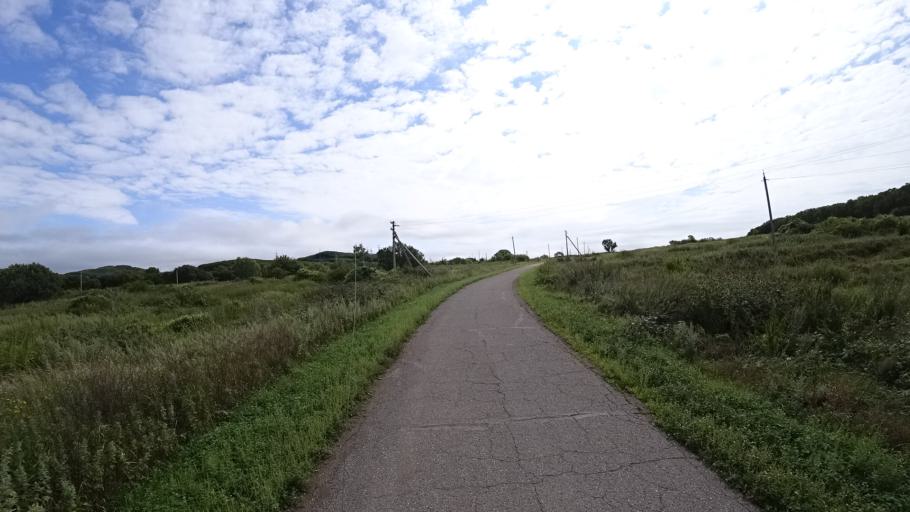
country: RU
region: Primorskiy
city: Lyalichi
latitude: 44.1351
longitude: 132.3878
